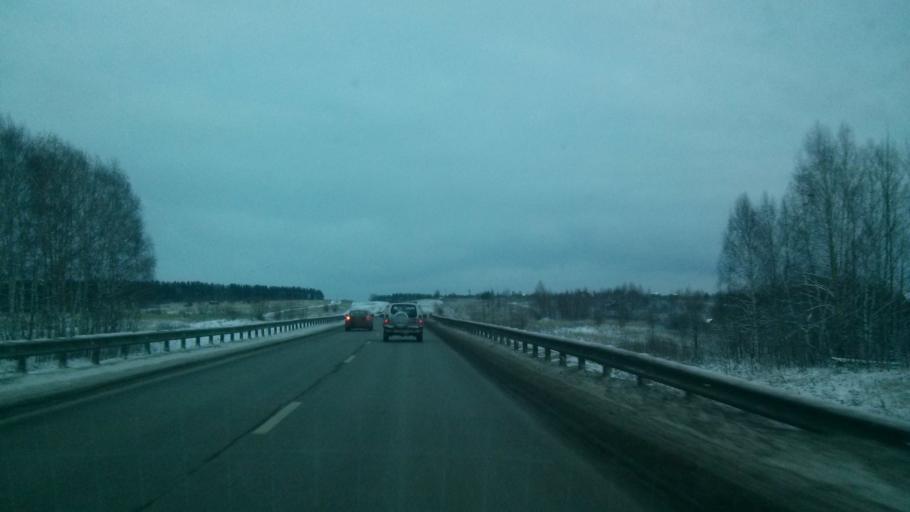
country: RU
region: Nizjnij Novgorod
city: Bogorodsk
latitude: 56.0873
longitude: 43.5479
